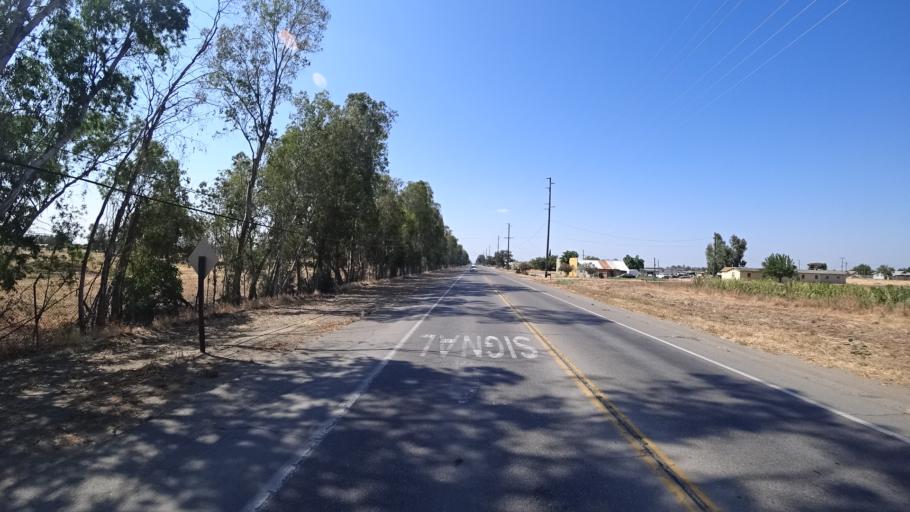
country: US
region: California
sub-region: Kings County
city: Home Garden
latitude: 36.3115
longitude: -119.6369
